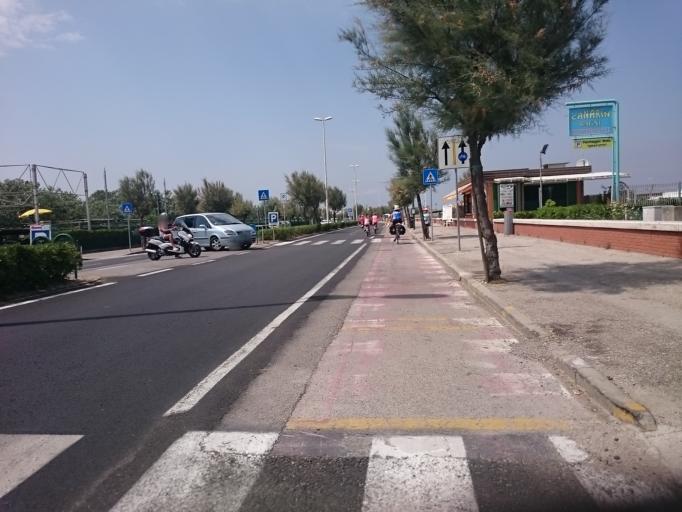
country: IT
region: Veneto
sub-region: Provincia di Venezia
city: Chioggia
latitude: 45.2056
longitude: 12.2990
